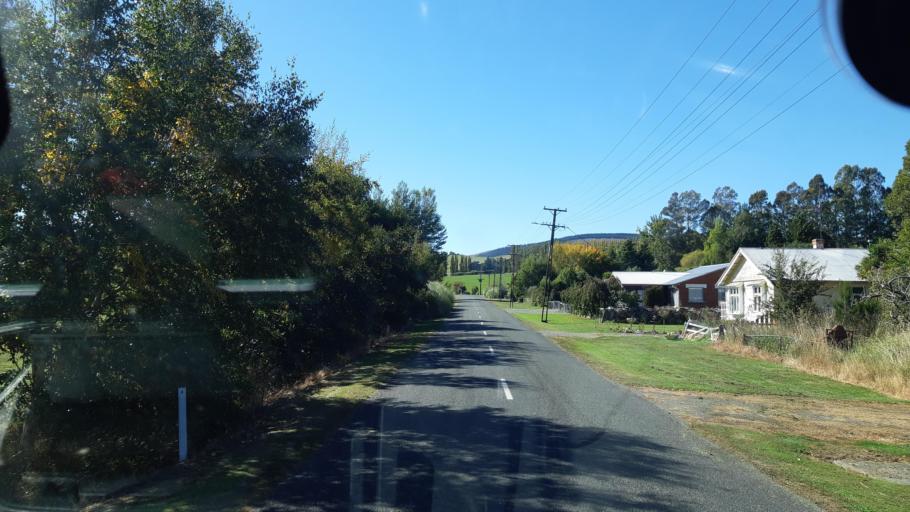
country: NZ
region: Southland
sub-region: Southland District
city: Winton
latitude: -45.8983
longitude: 168.3706
